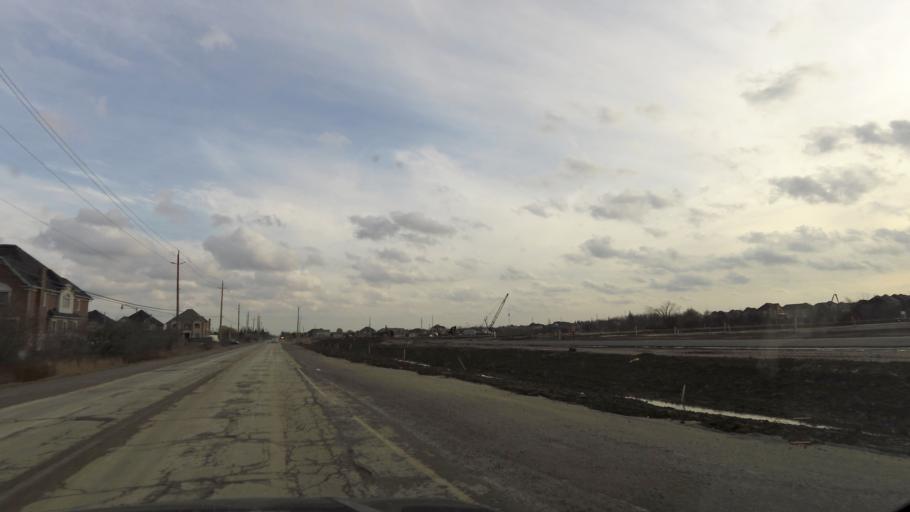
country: CA
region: Ontario
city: Brampton
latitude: 43.8047
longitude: -79.7306
